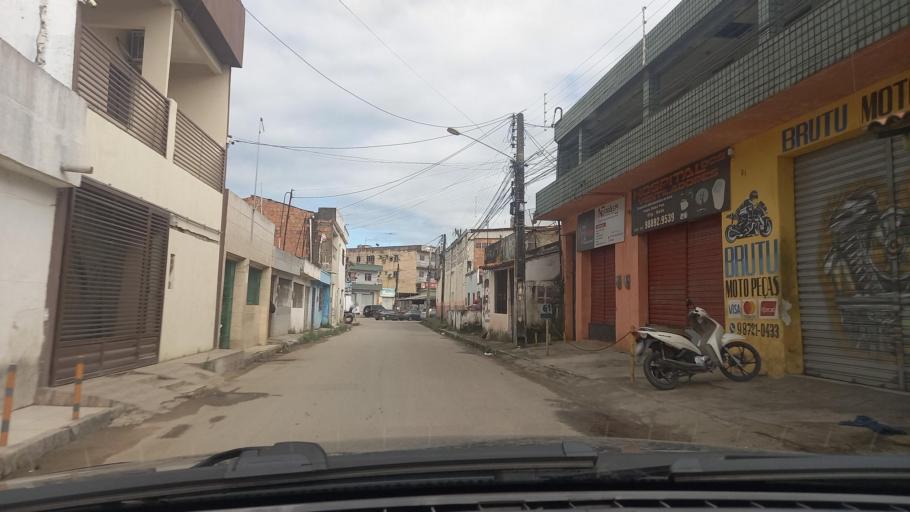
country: BR
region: Pernambuco
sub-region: Vitoria De Santo Antao
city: Vitoria de Santo Antao
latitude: -8.1216
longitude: -35.2935
